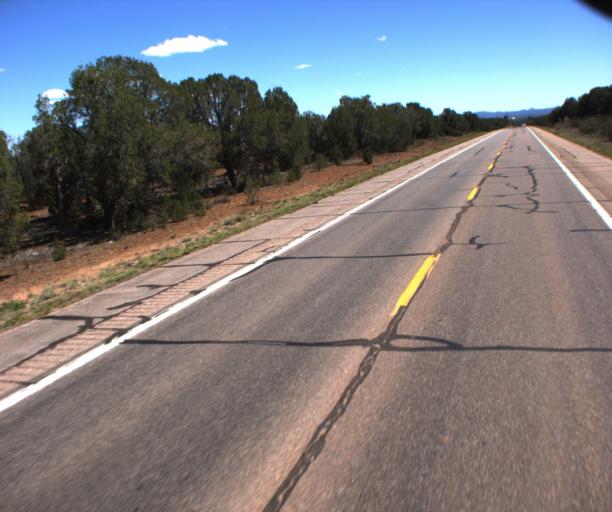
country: US
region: Arizona
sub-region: Yavapai County
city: Paulden
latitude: 35.0708
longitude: -112.4015
